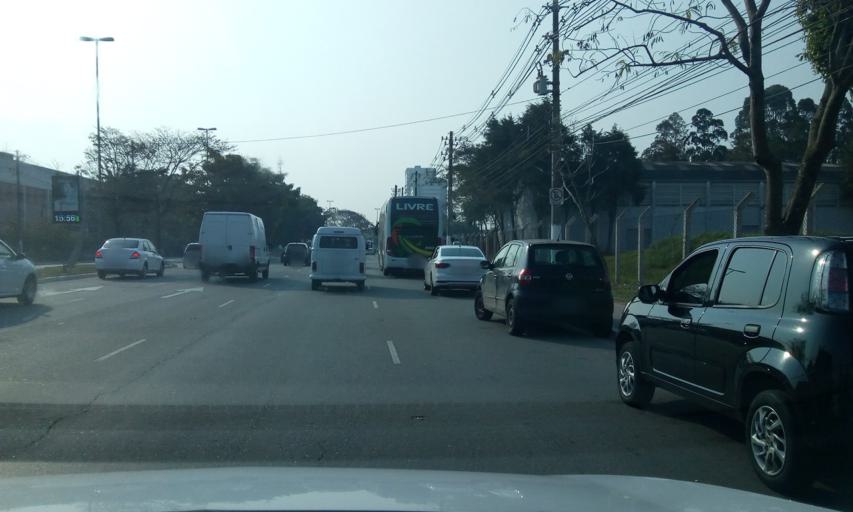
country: BR
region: Sao Paulo
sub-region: Diadema
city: Diadema
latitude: -23.6860
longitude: -46.6904
